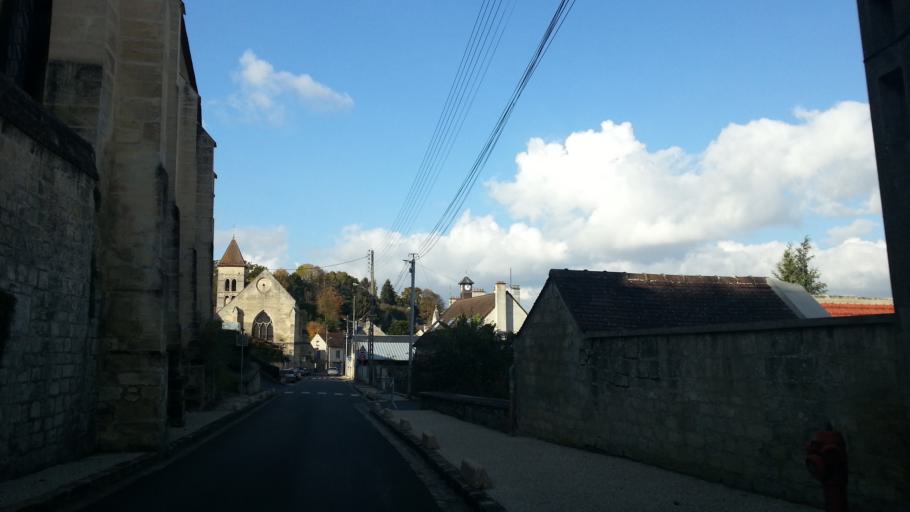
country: FR
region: Picardie
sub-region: Departement de l'Oise
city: Thiverny
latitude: 49.2542
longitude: 2.4024
